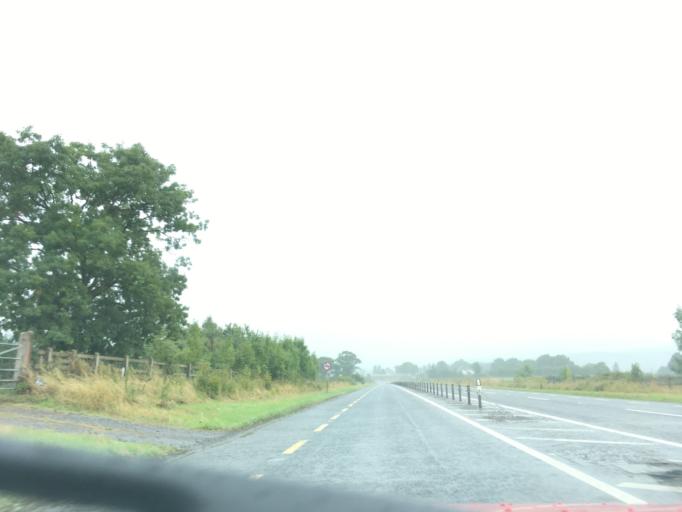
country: IE
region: Leinster
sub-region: Kilkenny
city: Piltown
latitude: 52.3515
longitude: -7.3393
